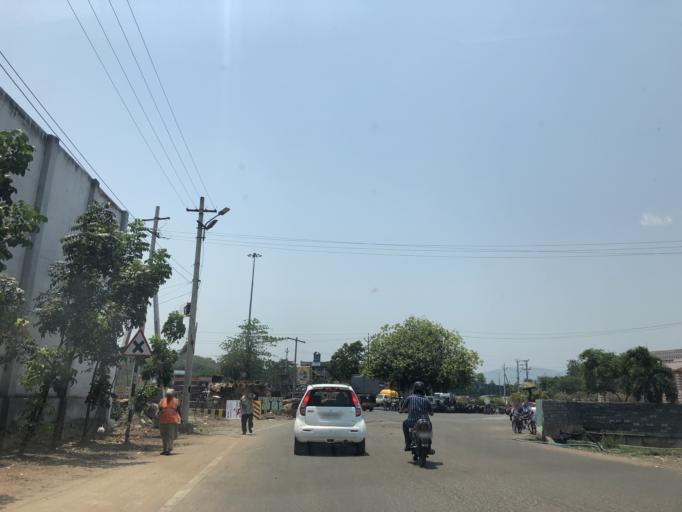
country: IN
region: Andhra Pradesh
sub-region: Vishakhapatnam
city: Yarada
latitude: 17.7169
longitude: 83.2906
